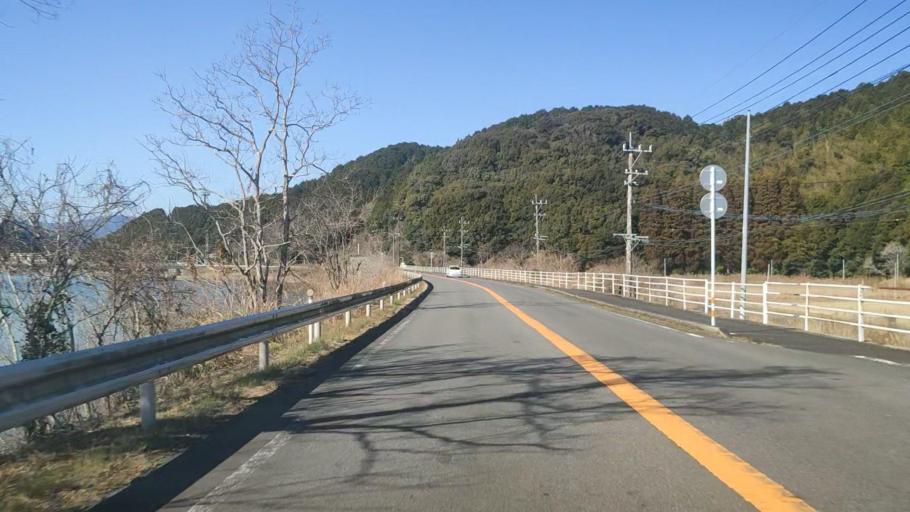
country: JP
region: Oita
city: Saiki
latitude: 32.9396
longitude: 131.9143
